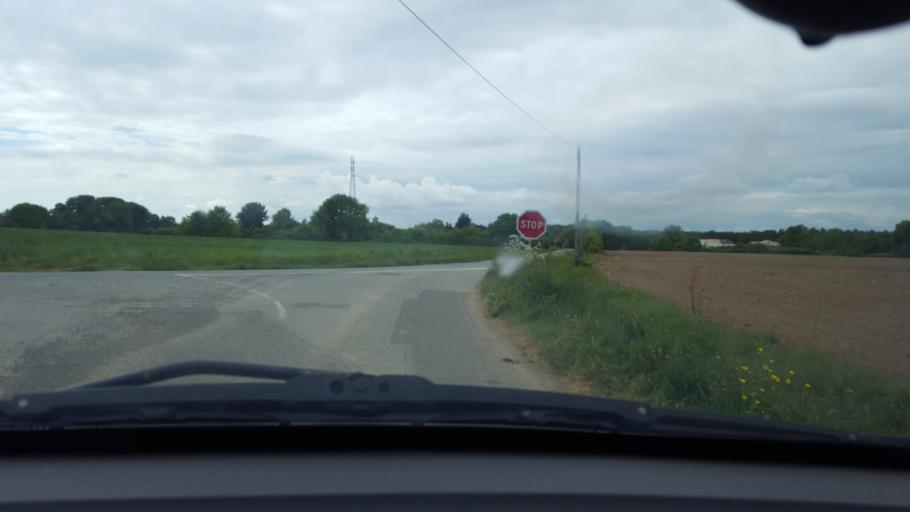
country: FR
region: Pays de la Loire
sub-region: Departement de la Loire-Atlantique
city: La Limouziniere
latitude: 47.0303
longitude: -1.6013
